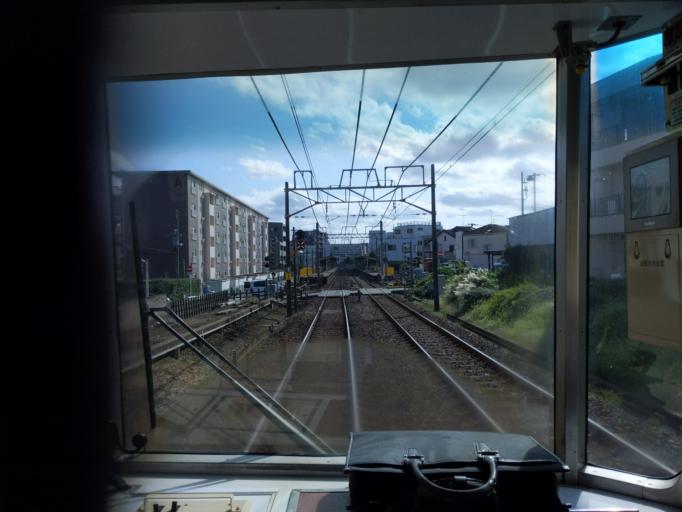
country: JP
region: Chiba
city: Funabashi
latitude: 35.7170
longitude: 140.0433
